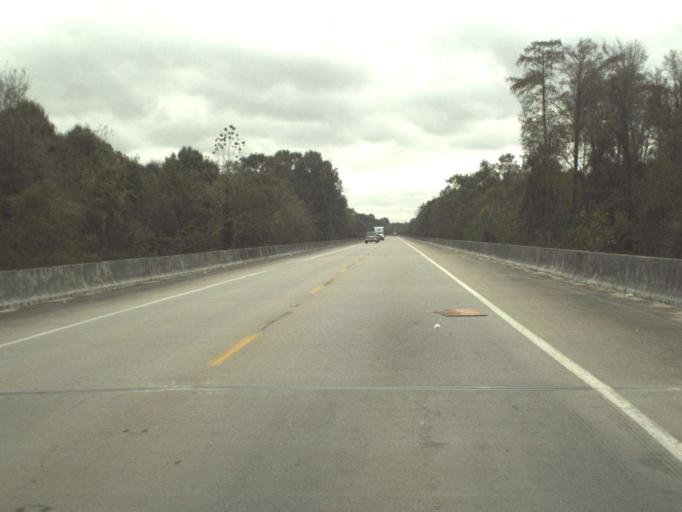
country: US
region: Florida
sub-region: Escambia County
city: Century
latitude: 30.9687
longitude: -87.2386
